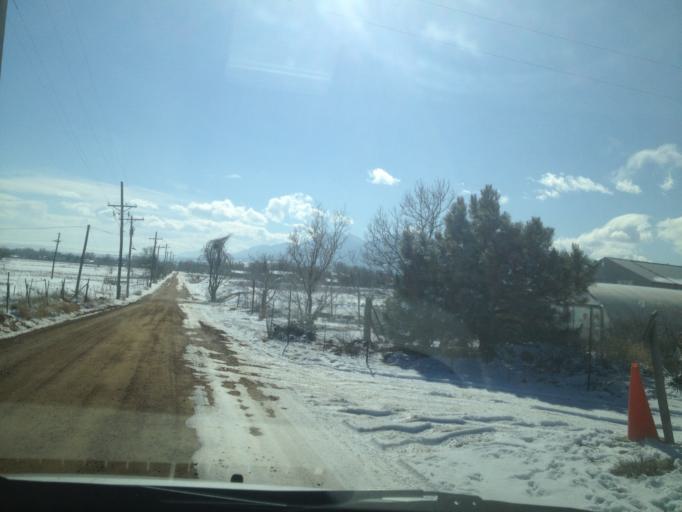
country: US
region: Colorado
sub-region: Boulder County
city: Boulder
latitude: 40.0614
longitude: -105.2634
